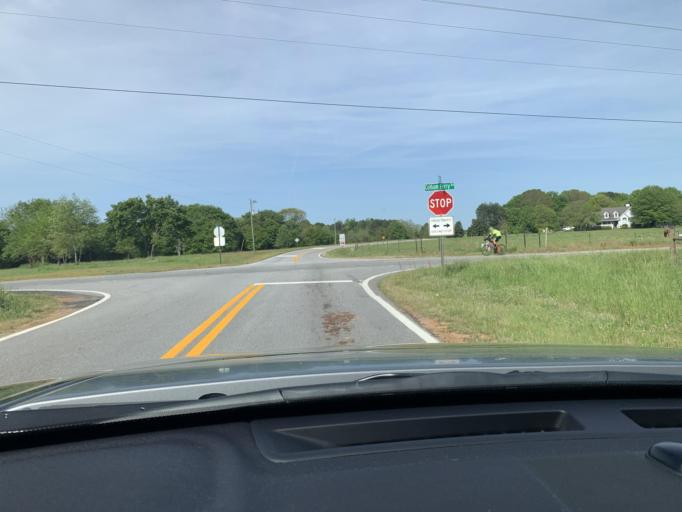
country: US
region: Georgia
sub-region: Oconee County
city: Watkinsville
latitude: 33.8119
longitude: -83.4011
